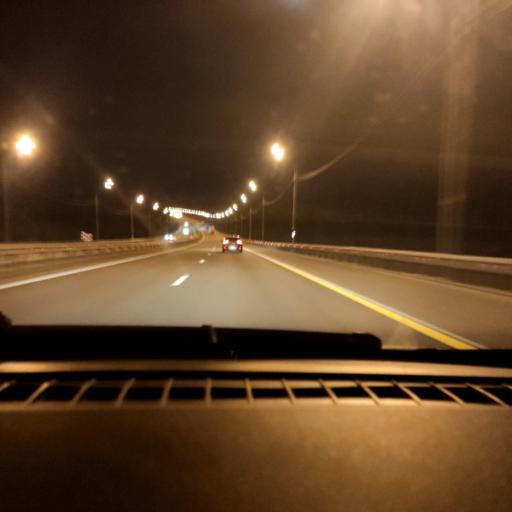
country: RU
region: Lipetsk
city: Khlevnoye
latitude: 52.2262
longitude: 39.1019
